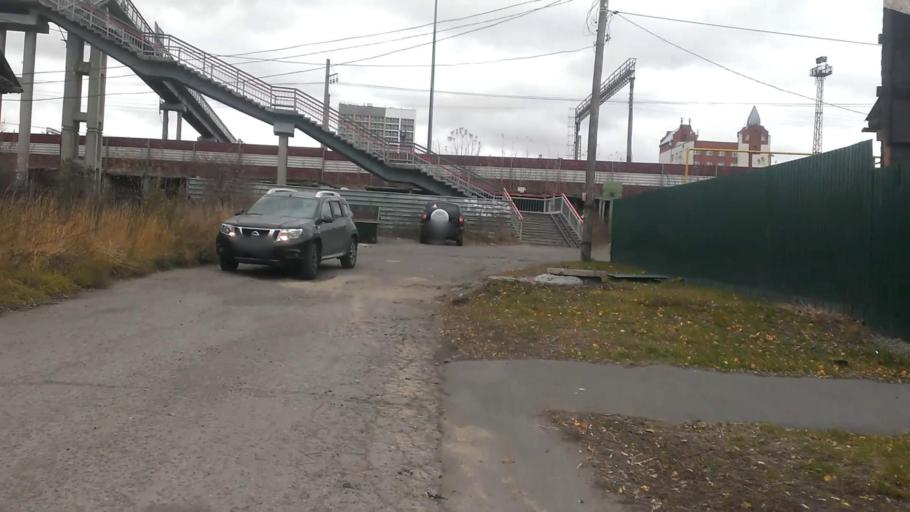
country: RU
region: Altai Krai
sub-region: Gorod Barnaulskiy
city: Barnaul
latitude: 53.3531
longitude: 83.7547
